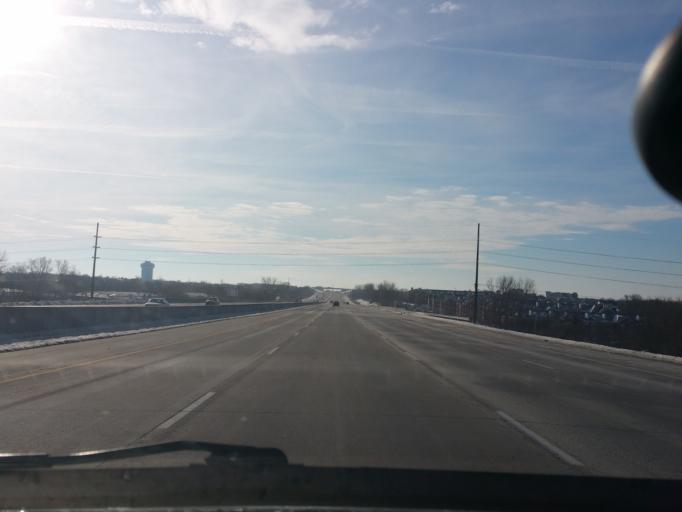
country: US
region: Iowa
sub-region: Polk County
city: Clive
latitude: 41.5769
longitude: -93.7774
